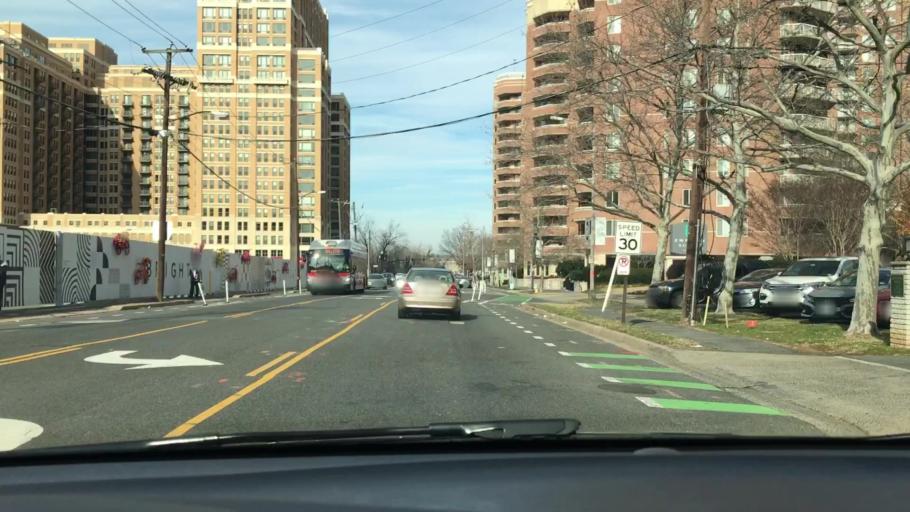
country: US
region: Washington, D.C.
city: Washington, D.C.
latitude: 38.8606
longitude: -77.0537
